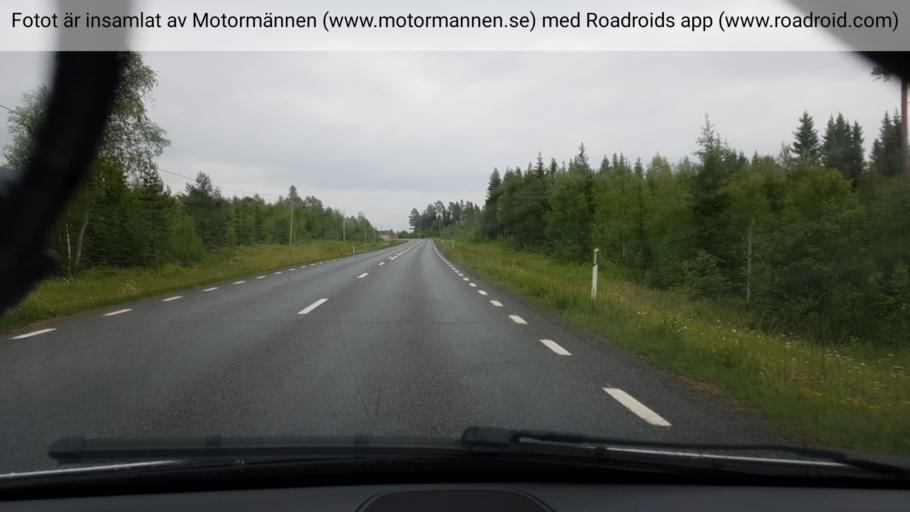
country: SE
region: Jaemtland
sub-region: OEstersunds Kommun
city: Lit
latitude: 63.3904
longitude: 14.9332
